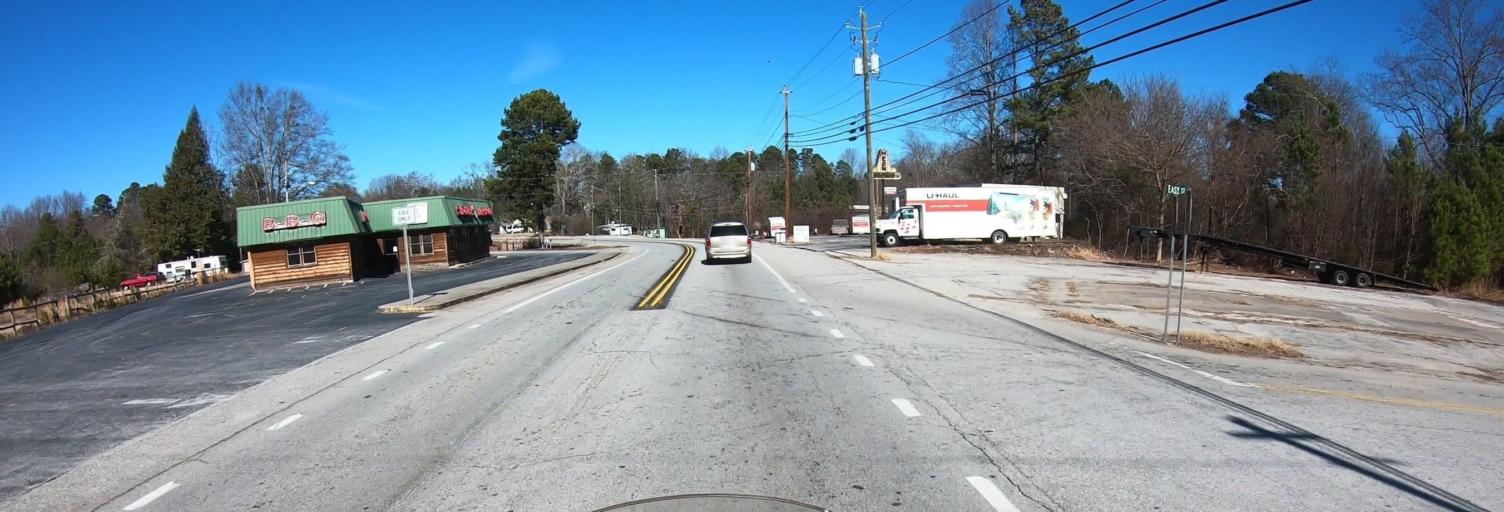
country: US
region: Georgia
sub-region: Stephens County
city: Toccoa
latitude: 34.5627
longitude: -83.3481
